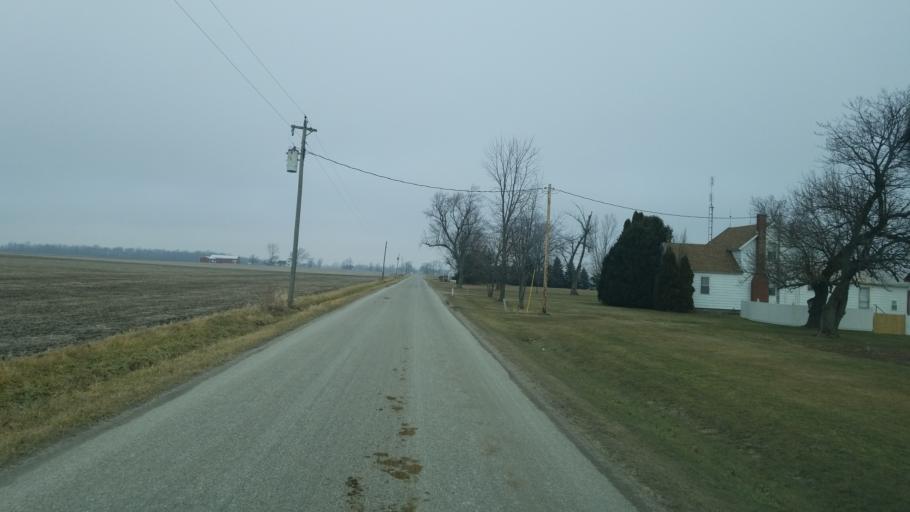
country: US
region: Indiana
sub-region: Adams County
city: Berne
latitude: 40.6825
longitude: -84.8549
